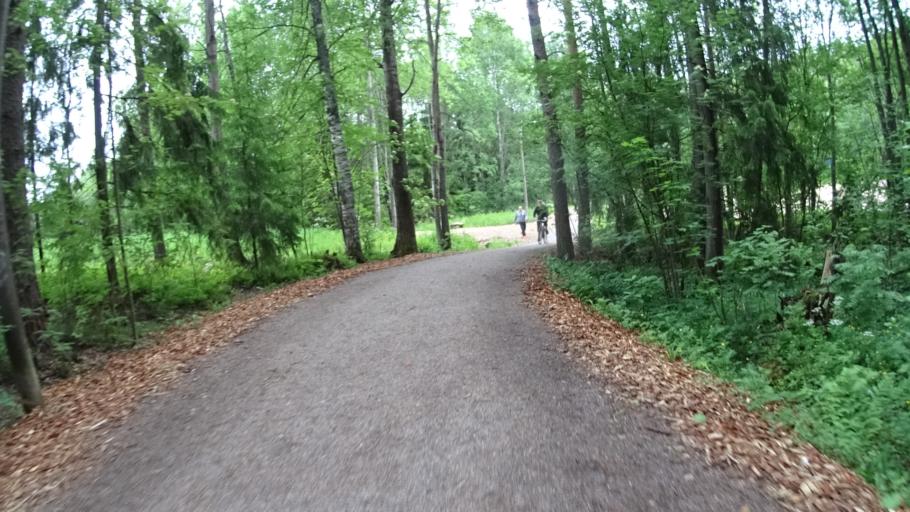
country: FI
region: Uusimaa
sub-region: Helsinki
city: Kilo
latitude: 60.2766
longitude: 24.8287
